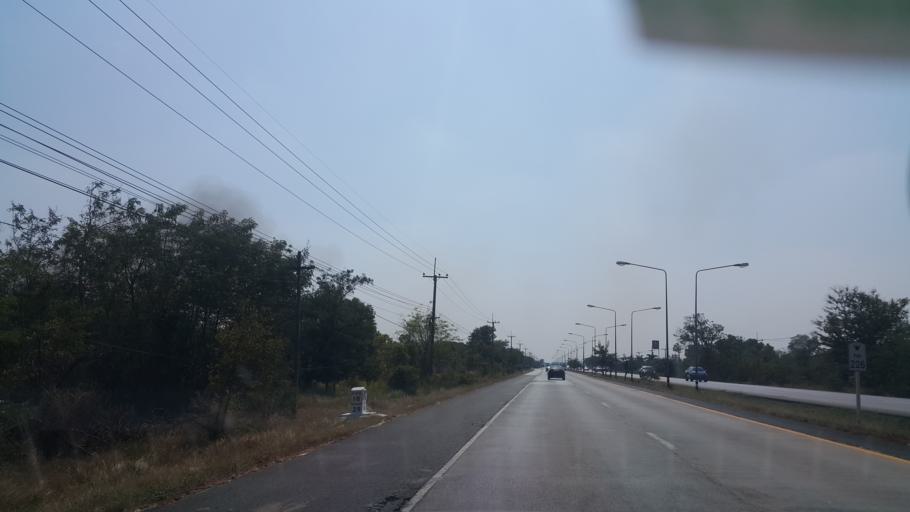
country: TH
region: Nakhon Ratchasima
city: Sida
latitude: 15.4909
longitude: 102.5223
